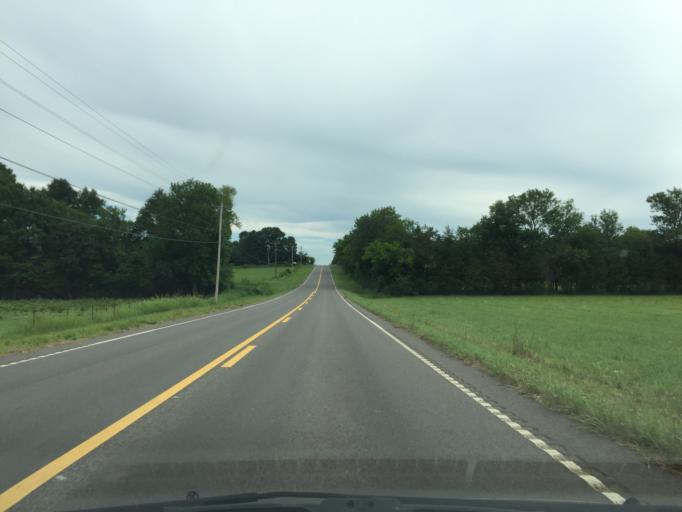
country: US
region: Tennessee
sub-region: Bradley County
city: Hopewell
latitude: 35.3407
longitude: -84.9256
